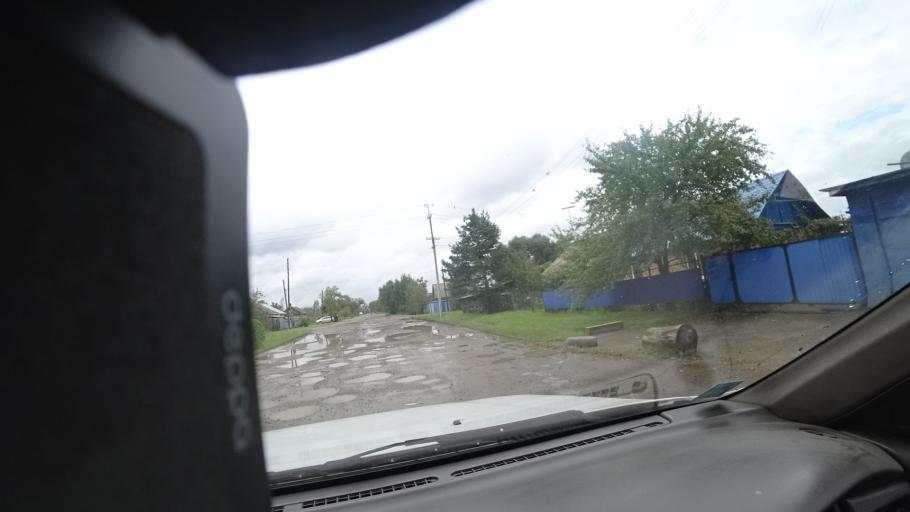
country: RU
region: Primorskiy
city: Dal'nerechensk
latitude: 45.9173
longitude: 133.7234
